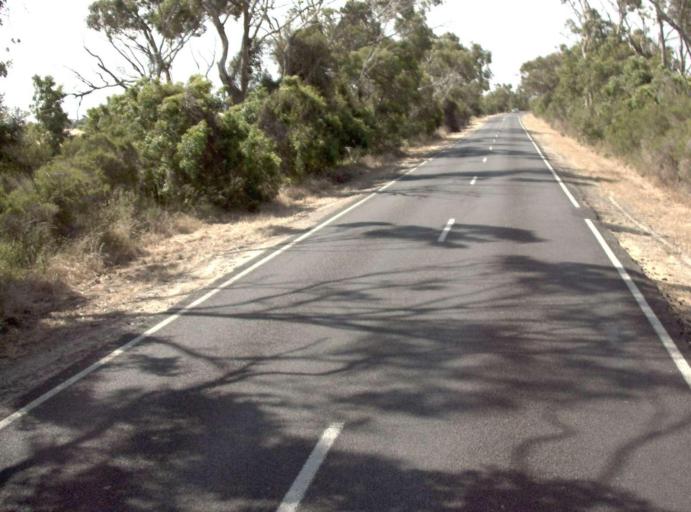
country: AU
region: Victoria
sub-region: Wellington
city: Sale
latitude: -38.3093
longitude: 147.1533
